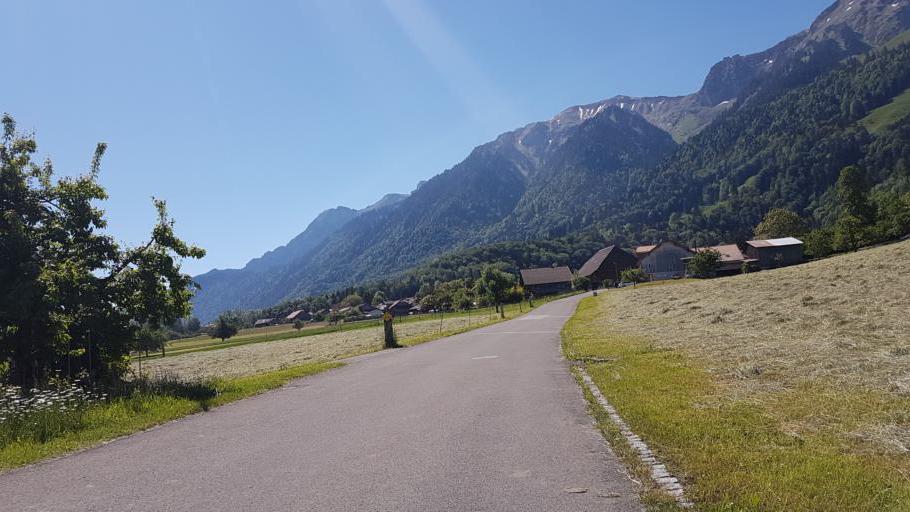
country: CH
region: Bern
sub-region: Thun District
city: Blumenstein
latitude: 46.7345
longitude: 7.5121
